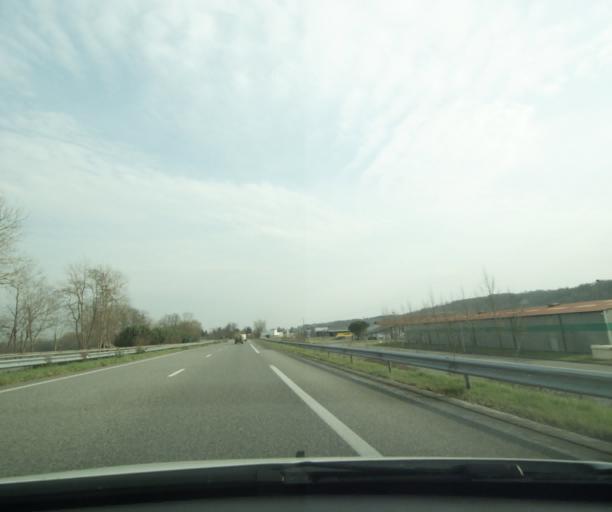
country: FR
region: Aquitaine
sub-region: Departement des Pyrenees-Atlantiques
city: Orthez
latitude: 43.4725
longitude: -0.7572
